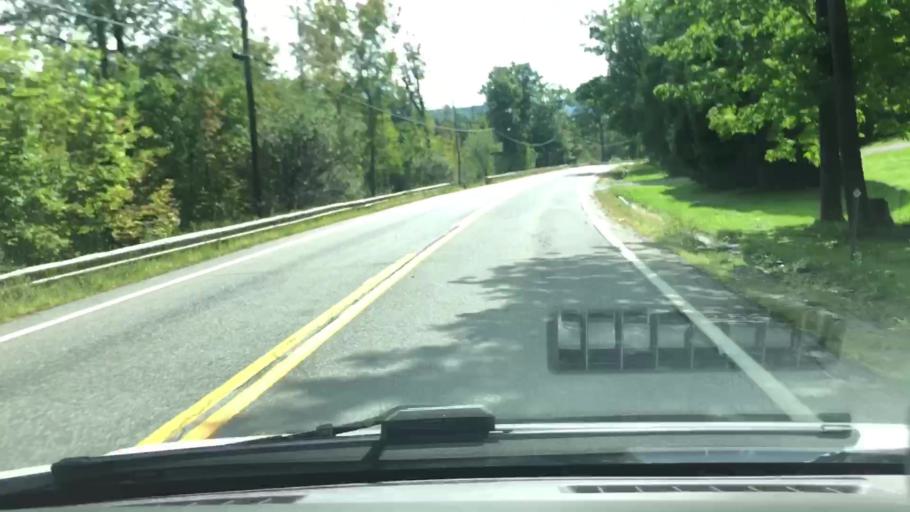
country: US
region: Massachusetts
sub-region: Berkshire County
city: North Adams
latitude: 42.6561
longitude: -73.0012
